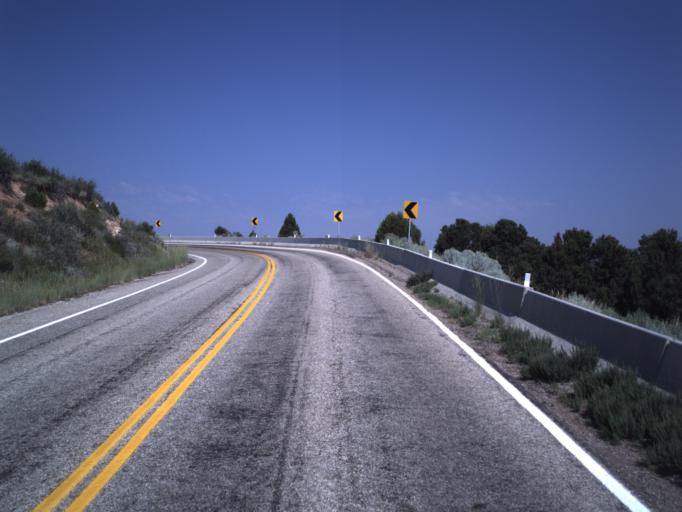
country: US
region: Utah
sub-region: Daggett County
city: Manila
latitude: 40.8974
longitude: -109.4539
